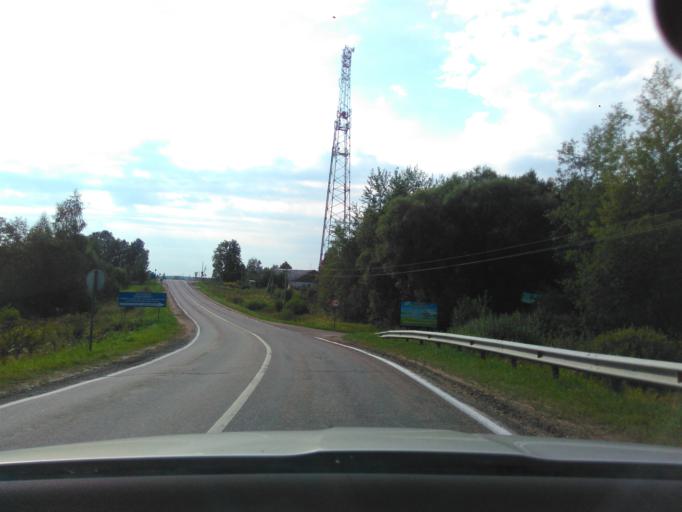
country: RU
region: Moskovskaya
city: Klin
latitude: 56.1463
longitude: 36.7861
